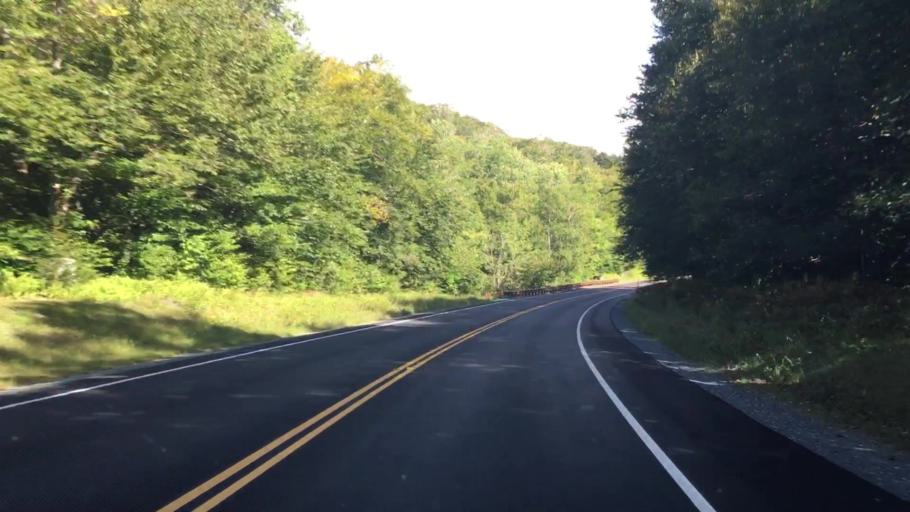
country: US
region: New Hampshire
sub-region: Grafton County
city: Woodstock
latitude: 44.0267
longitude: -71.7558
